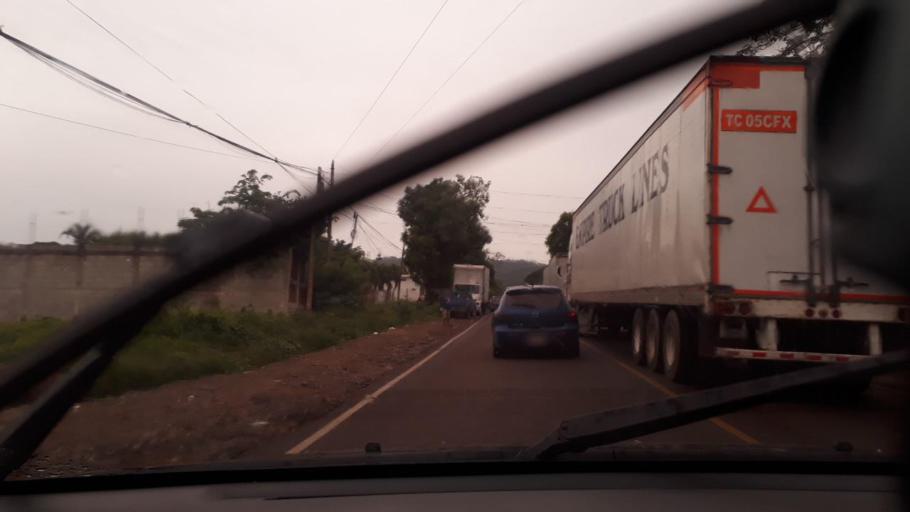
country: GT
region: Jutiapa
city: Atescatempa
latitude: 14.1925
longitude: -89.6721
